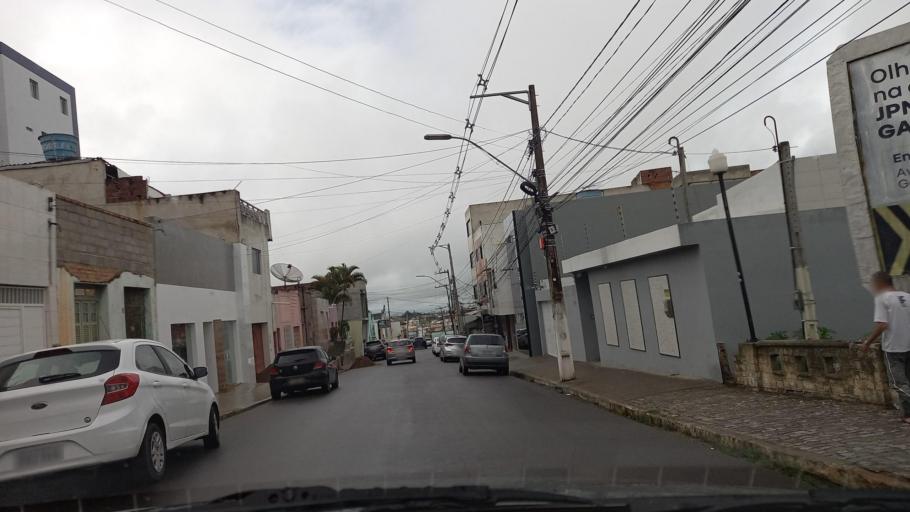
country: BR
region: Pernambuco
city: Garanhuns
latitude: -8.8874
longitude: -36.4982
